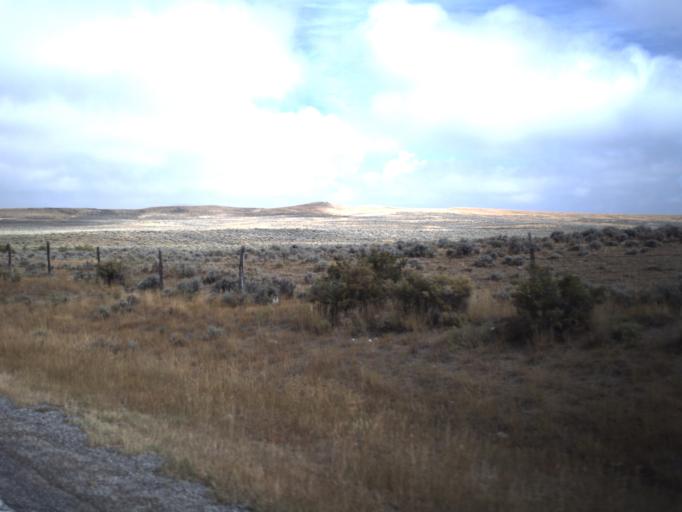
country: US
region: Utah
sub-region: Rich County
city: Randolph
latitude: 41.4683
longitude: -111.1053
